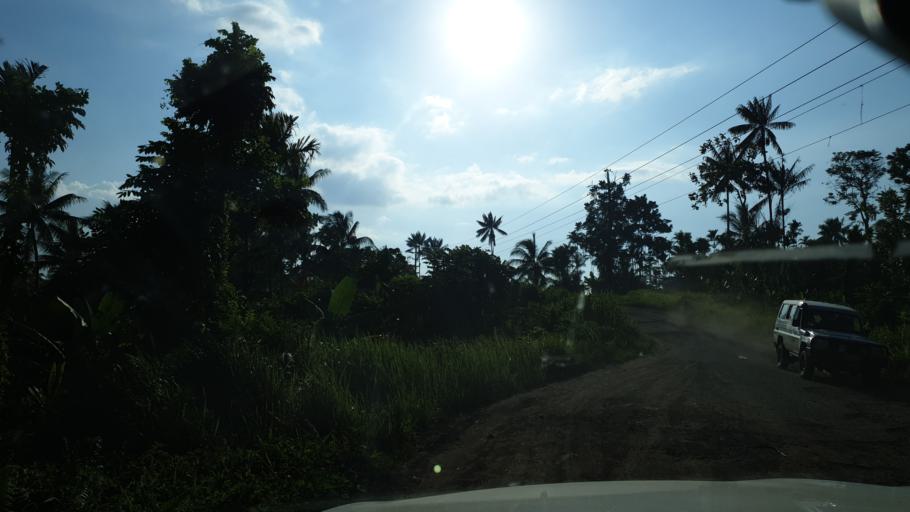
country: PG
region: East Sepik
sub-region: Wewak
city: Wewak
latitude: -3.7035
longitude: 143.6421
